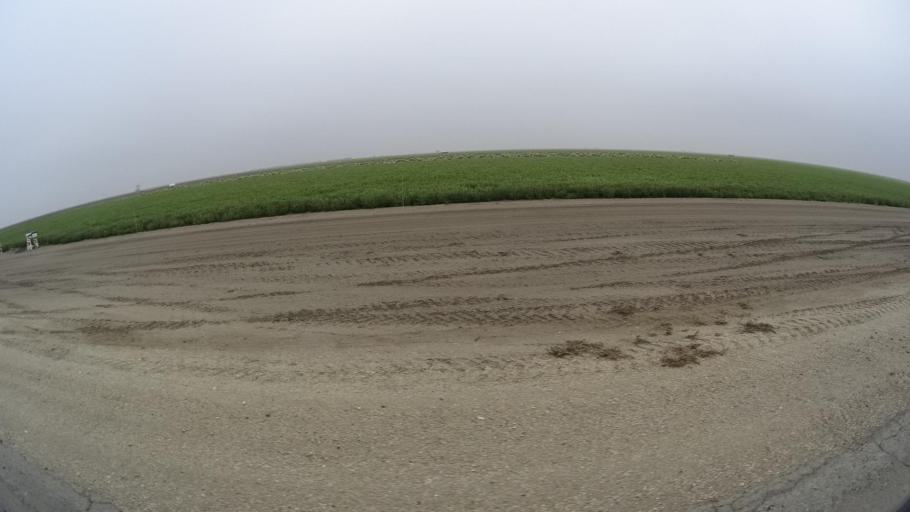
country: US
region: California
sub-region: Kern County
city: Rosedale
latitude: 35.1944
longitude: -119.2009
